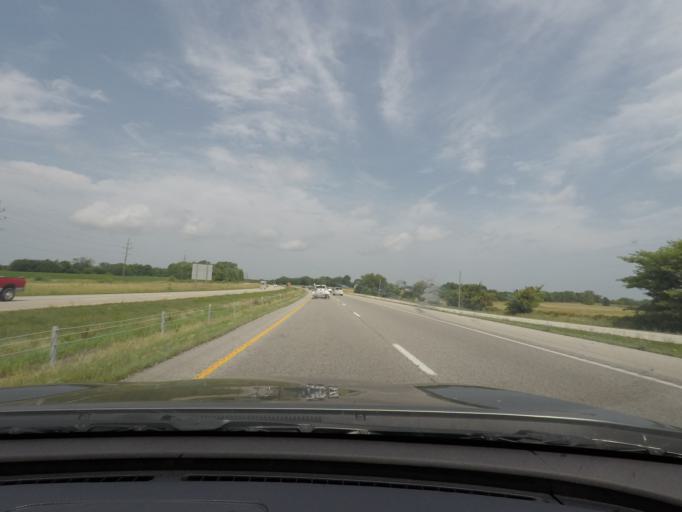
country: US
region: Missouri
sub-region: Warren County
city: Warrenton
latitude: 38.8431
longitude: -91.2297
